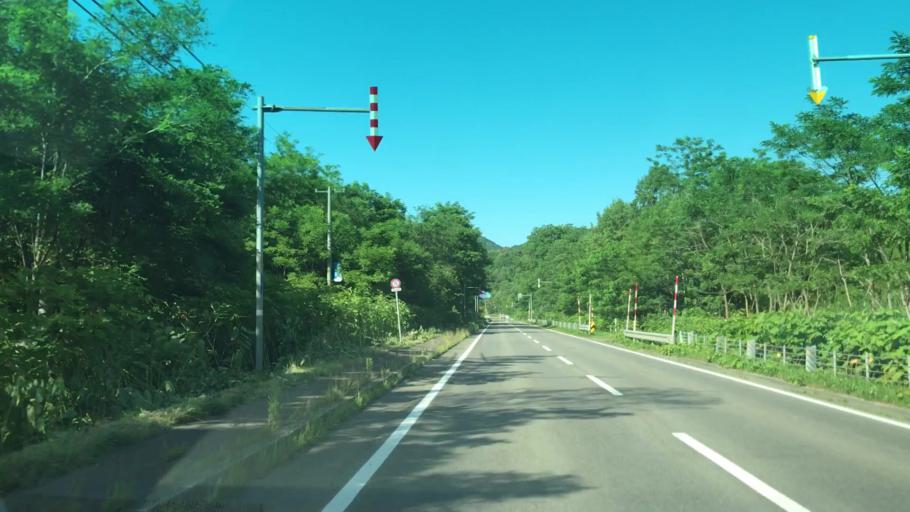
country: JP
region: Hokkaido
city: Iwanai
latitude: 42.9923
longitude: 140.6635
